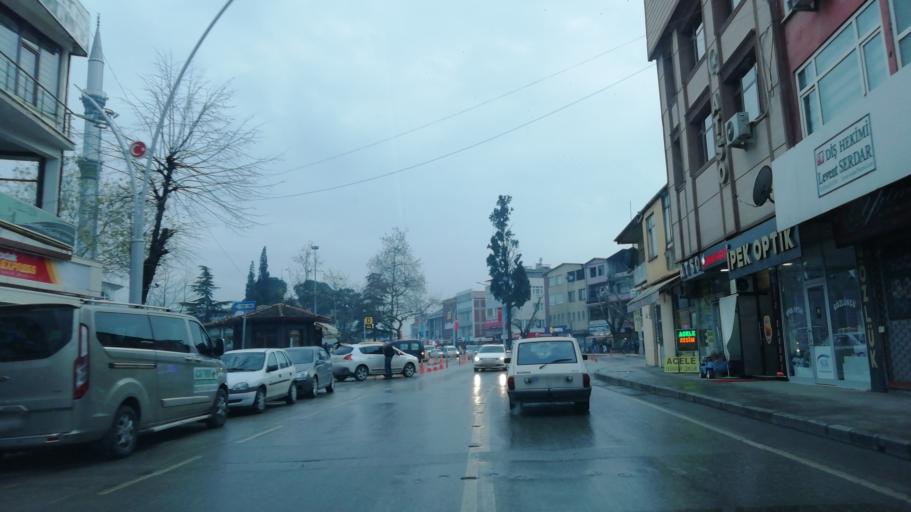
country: TR
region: Sakarya
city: Akyazi
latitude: 40.6819
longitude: 30.6249
